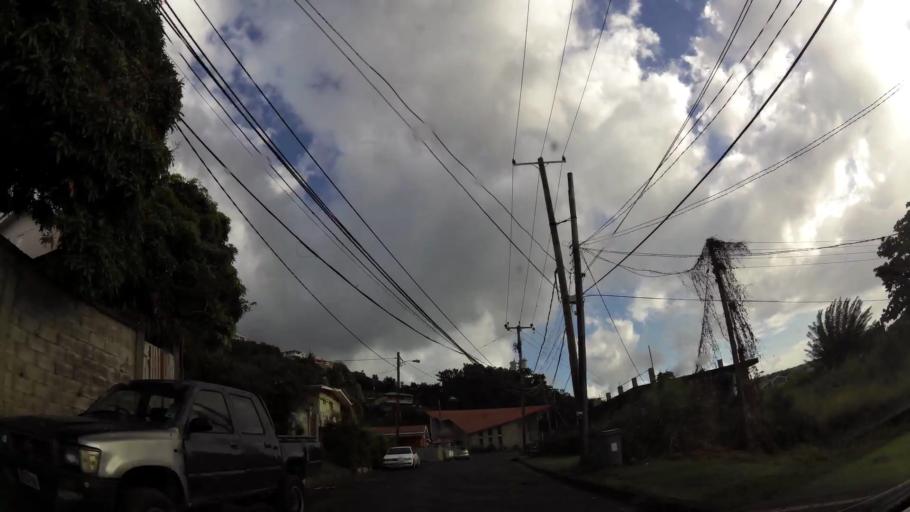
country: DM
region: Saint Paul
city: Mahaut
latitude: 15.3365
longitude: -61.3900
